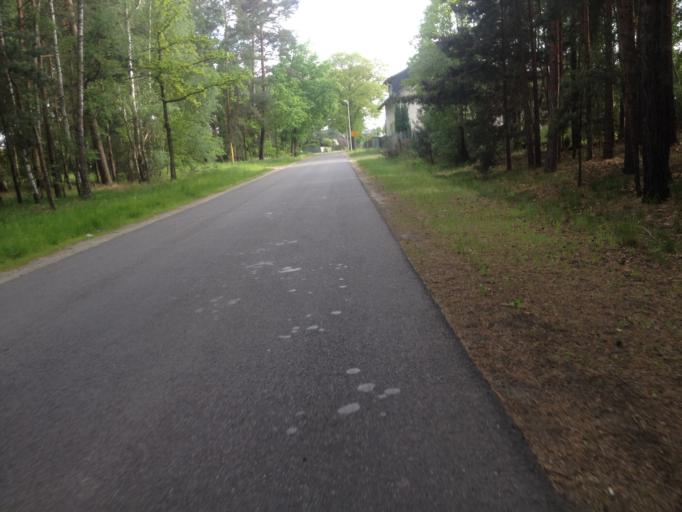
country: DE
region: Brandenburg
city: Cottbus
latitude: 51.8054
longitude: 14.3120
